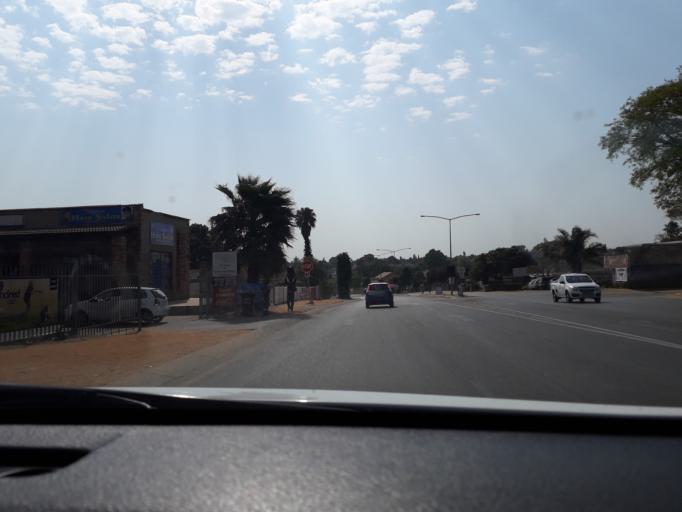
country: ZA
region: Gauteng
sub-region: Ekurhuleni Metropolitan Municipality
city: Tembisa
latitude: -26.0784
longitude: 28.2505
